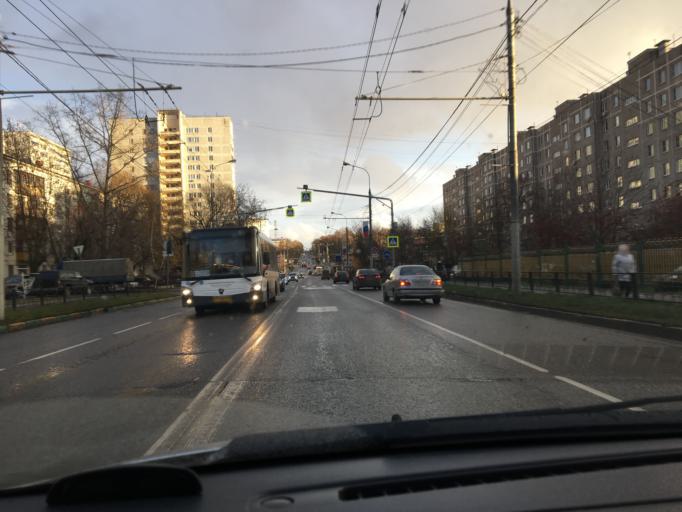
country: RU
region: Moskovskaya
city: Vidnoye
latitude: 55.5535
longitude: 37.6990
